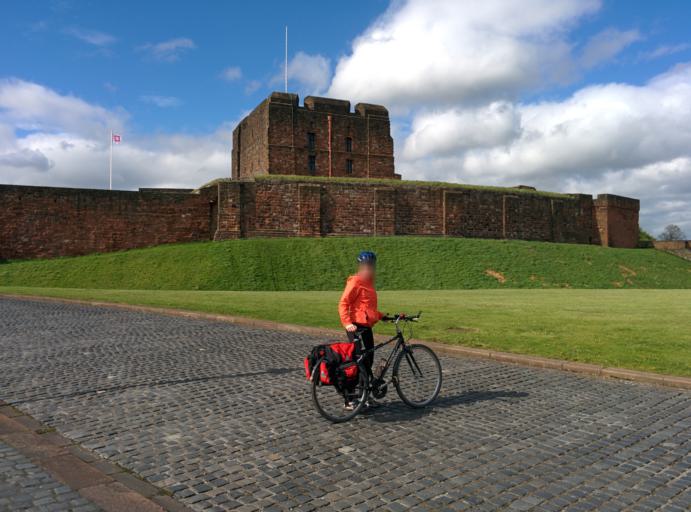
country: GB
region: England
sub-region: Cumbria
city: Carlisle
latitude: 54.8962
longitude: -2.9407
